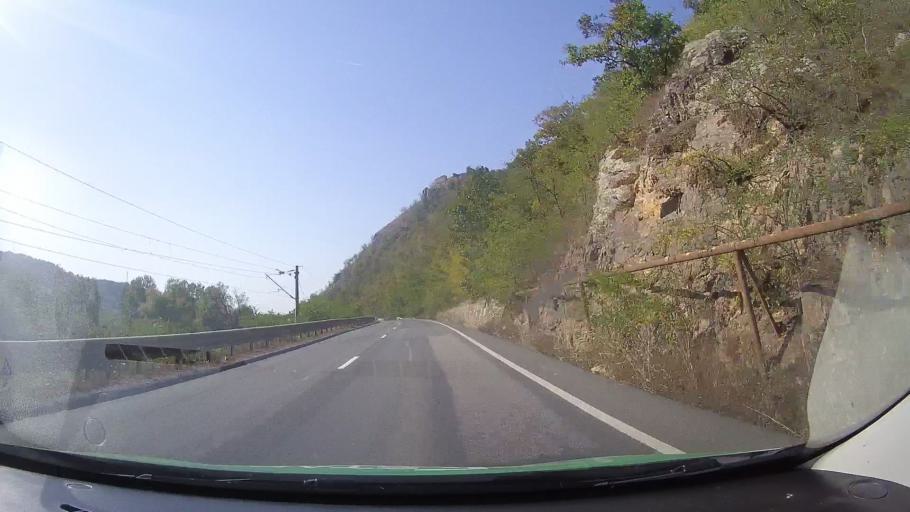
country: RO
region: Arad
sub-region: Oras Lipova
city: Lipova
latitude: 46.1089
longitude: 21.7292
